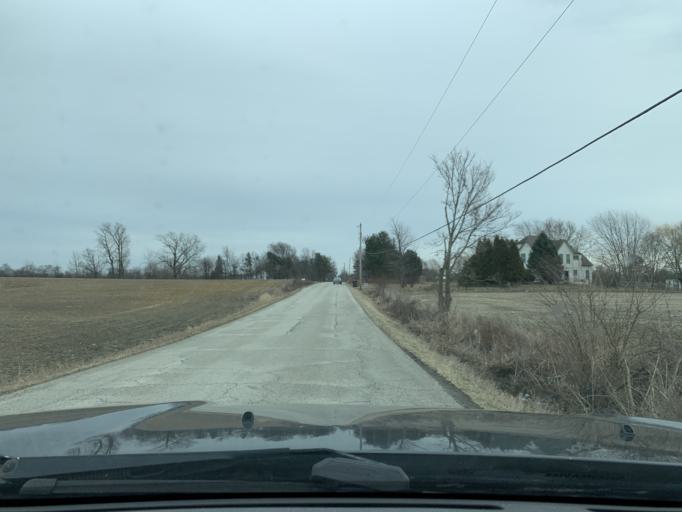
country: US
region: Indiana
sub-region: Porter County
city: Chesterton
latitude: 41.5862
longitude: -87.0264
